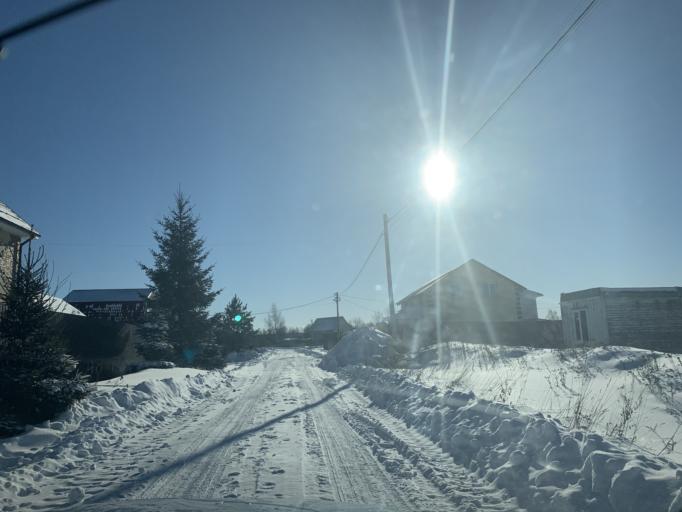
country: RU
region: Jaroslavl
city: Tunoshna
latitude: 57.6639
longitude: 40.0666
